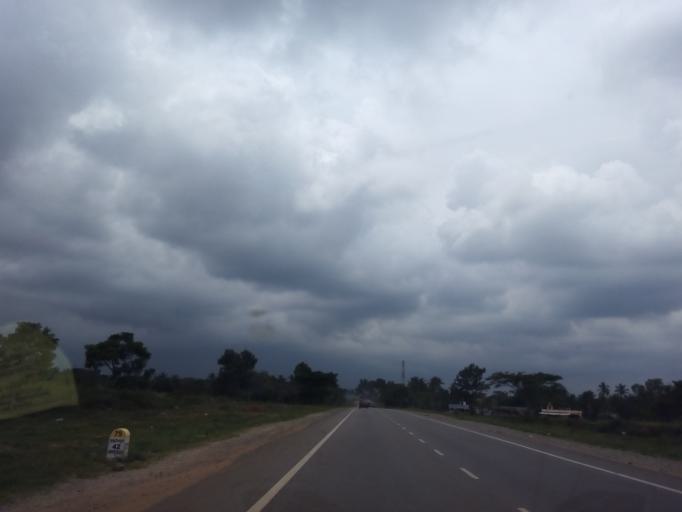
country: IN
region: Karnataka
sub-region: Hassan
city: Hassan
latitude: 13.0004
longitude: 76.1318
